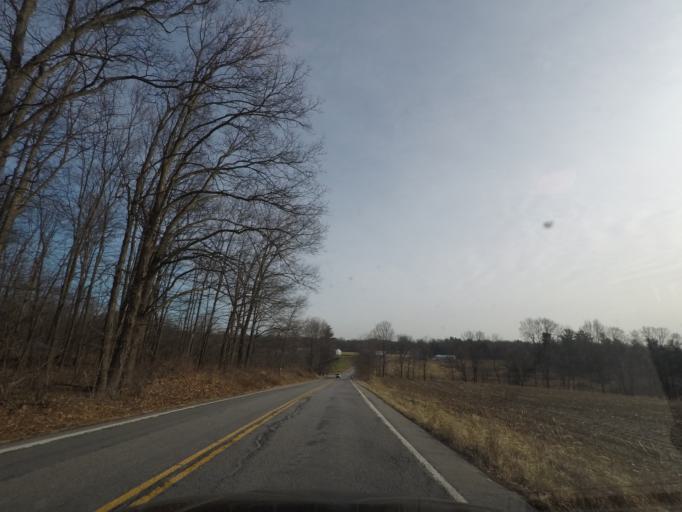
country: US
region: New York
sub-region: Saratoga County
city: Stillwater
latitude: 42.9882
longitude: -73.6918
